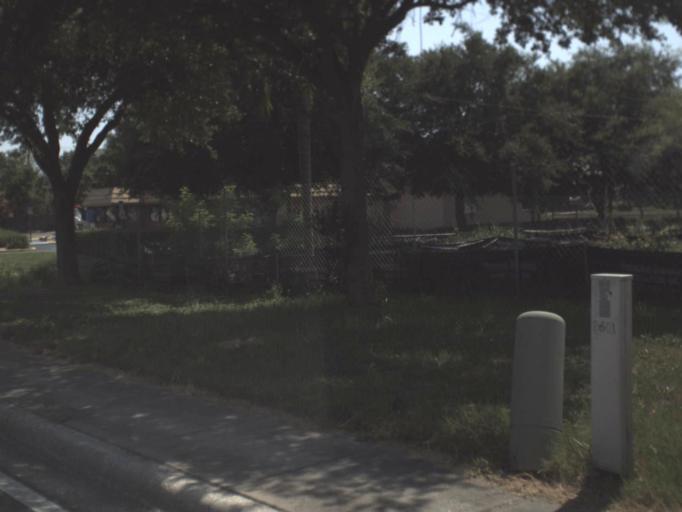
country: US
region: Florida
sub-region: Pinellas County
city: Gulfport
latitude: 27.7441
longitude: -82.6794
